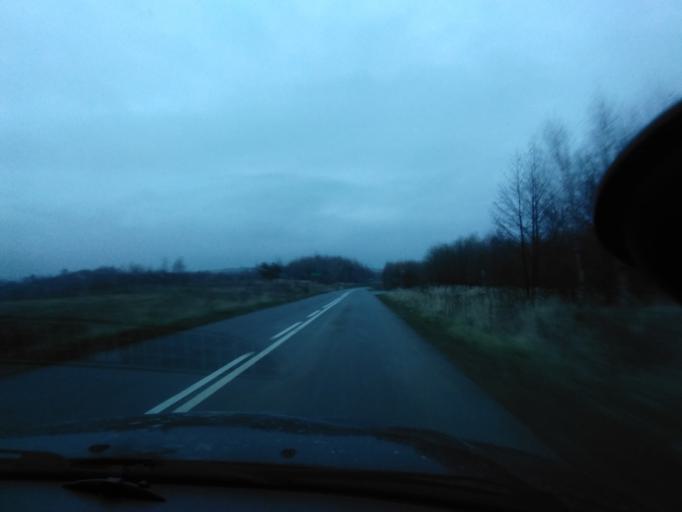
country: PL
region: Subcarpathian Voivodeship
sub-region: Powiat jaroslawski
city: Jodlowka
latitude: 49.8851
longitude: 22.4699
